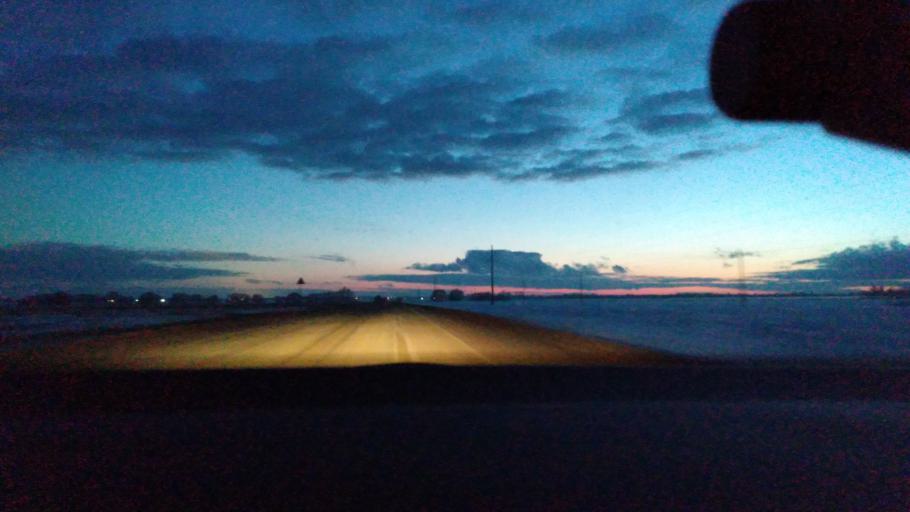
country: RU
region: Moskovskaya
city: Krasnaya Poyma
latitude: 55.0857
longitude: 39.1436
